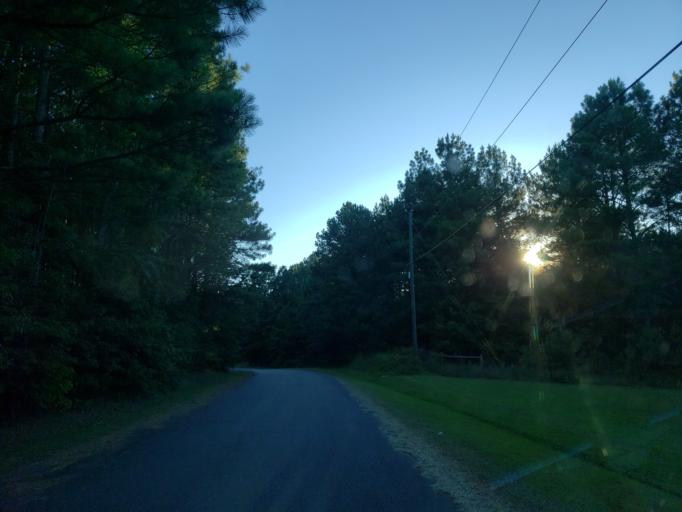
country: US
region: Georgia
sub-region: Bartow County
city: Euharlee
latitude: 34.0965
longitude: -84.9683
